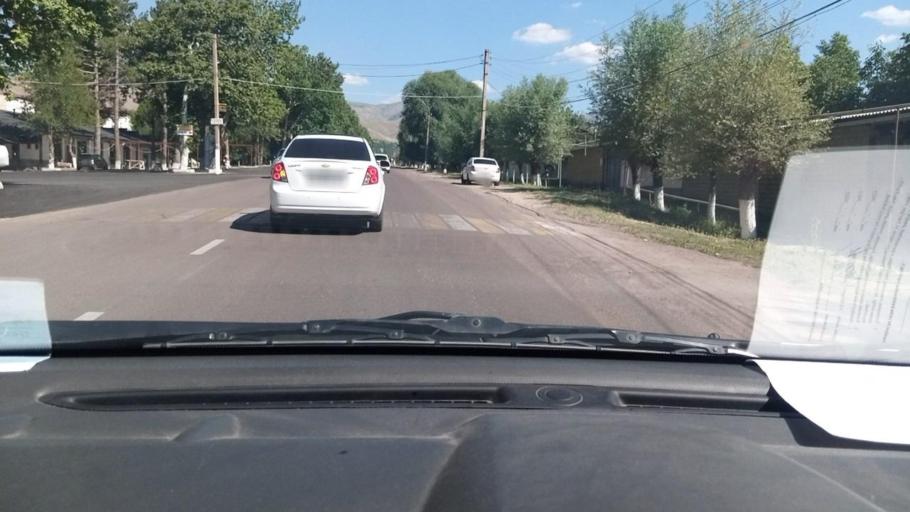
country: UZ
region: Toshkent
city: Angren
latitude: 41.0405
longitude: 70.0932
